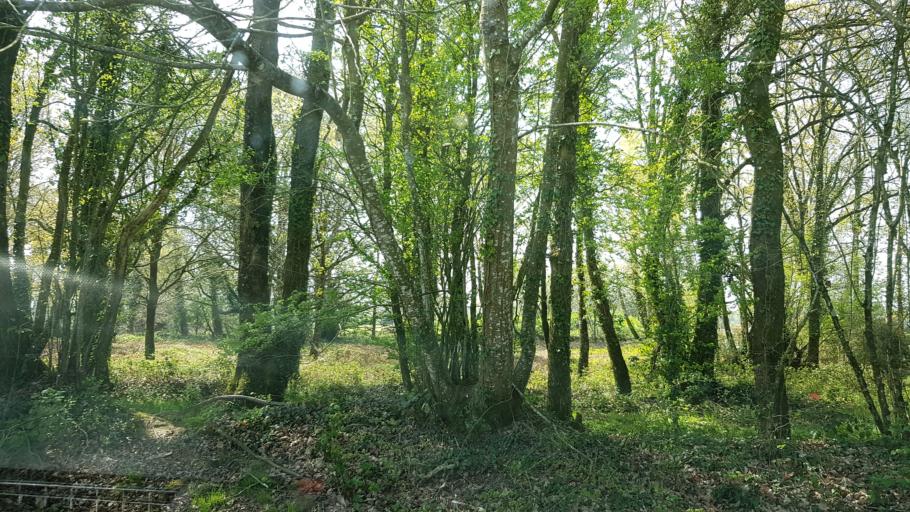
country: FR
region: Brittany
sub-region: Departement du Morbihan
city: Peaule
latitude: 47.5911
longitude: -2.4022
